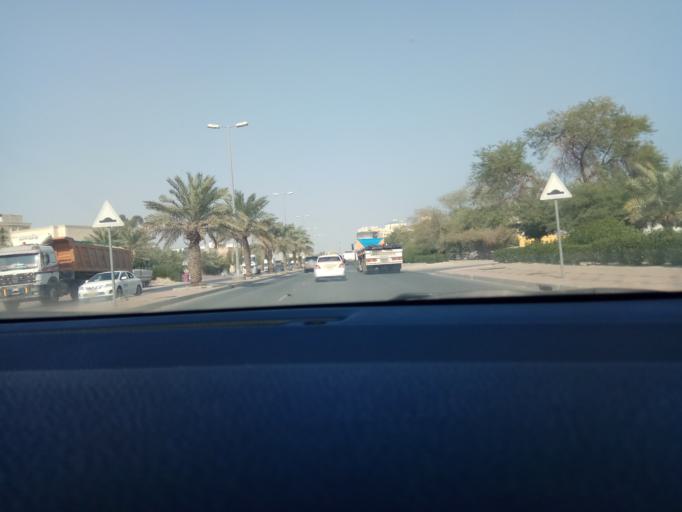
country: KW
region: Al Ahmadi
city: Al Fahahil
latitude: 29.0753
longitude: 48.1250
